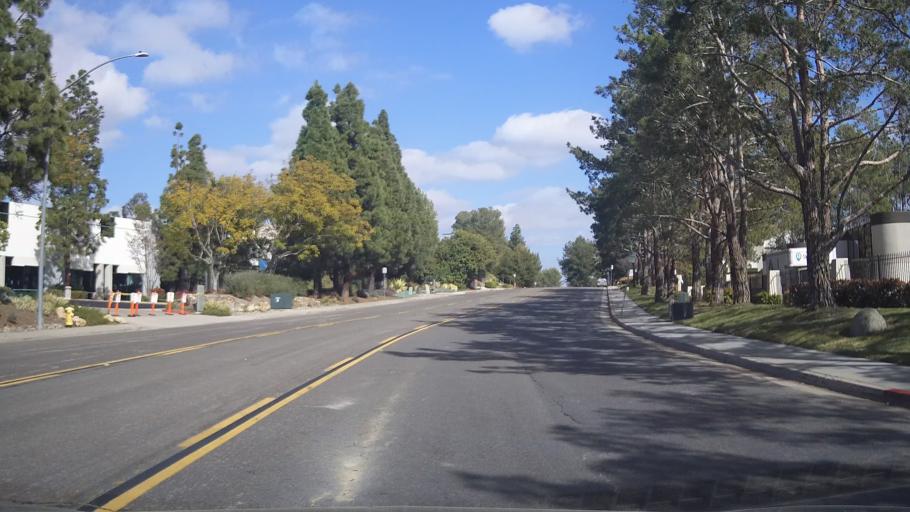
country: US
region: California
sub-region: San Diego County
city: Poway
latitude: 32.9879
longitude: -117.0717
